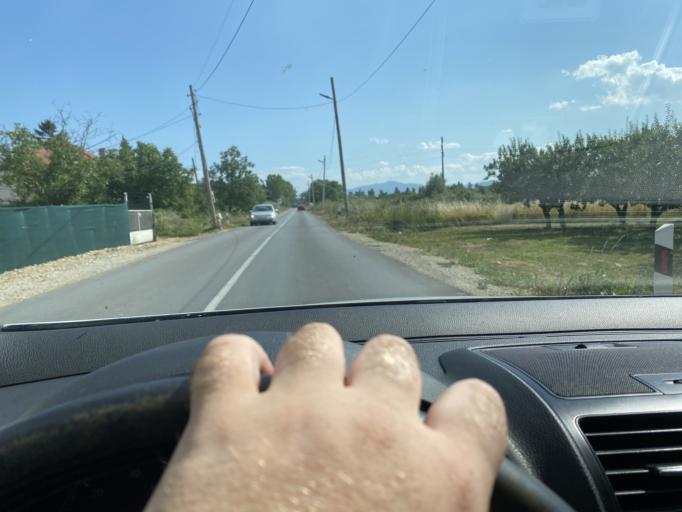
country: MK
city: Misleshevo
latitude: 41.1761
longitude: 20.7068
